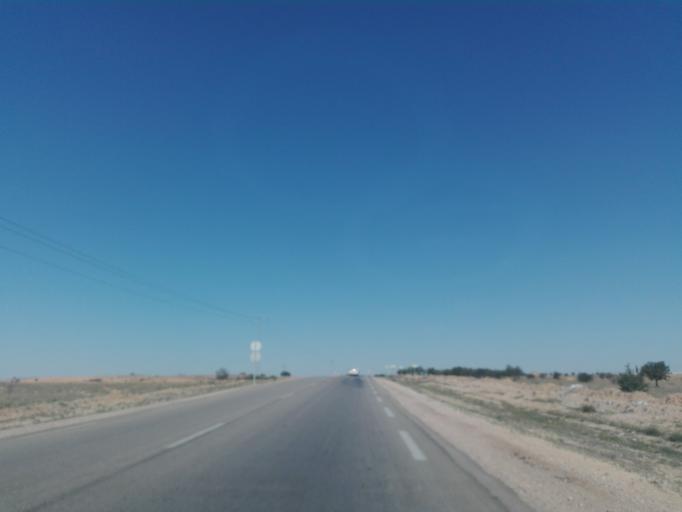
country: TN
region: Safaqis
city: Bi'r `Ali Bin Khalifah
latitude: 34.7365
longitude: 10.4113
